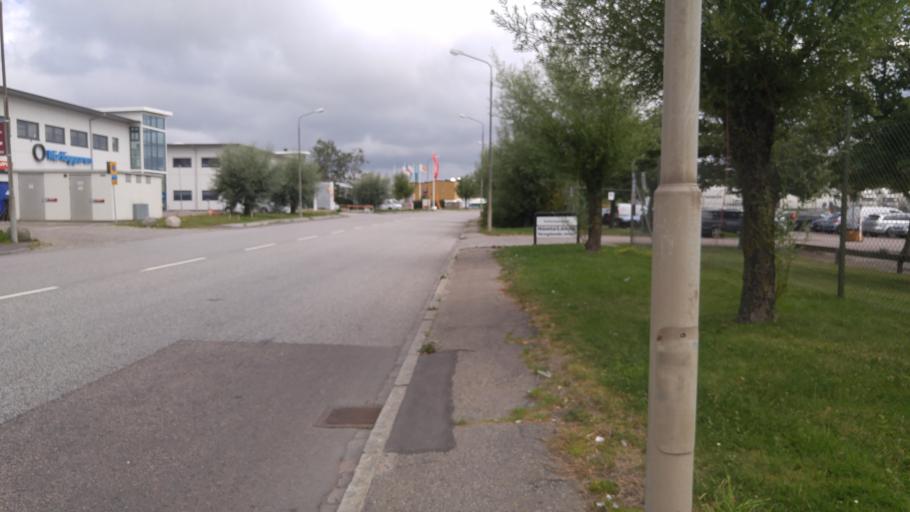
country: SE
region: Skane
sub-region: Malmo
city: Oxie
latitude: 55.5560
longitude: 13.0464
